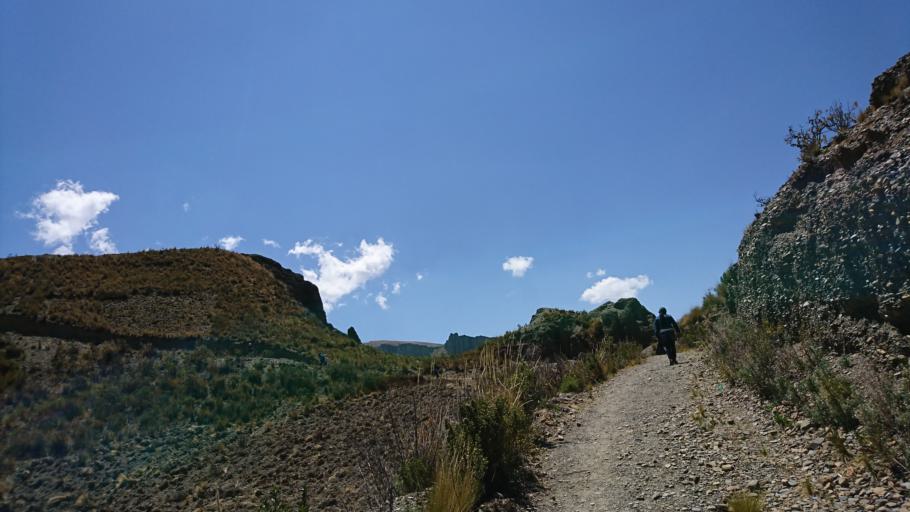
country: BO
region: La Paz
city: La Paz
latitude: -16.5446
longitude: -68.0107
